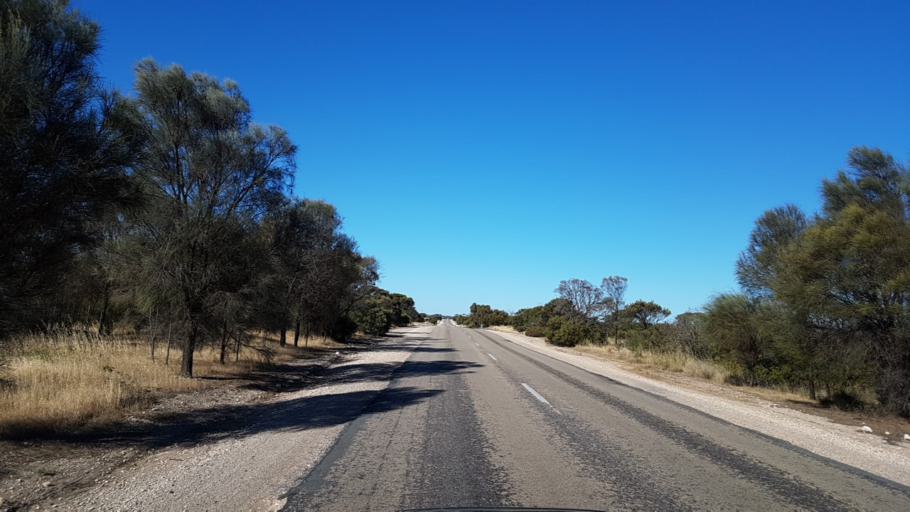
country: AU
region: South Australia
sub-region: Yorke Peninsula
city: Honiton
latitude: -34.8534
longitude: 137.5109
